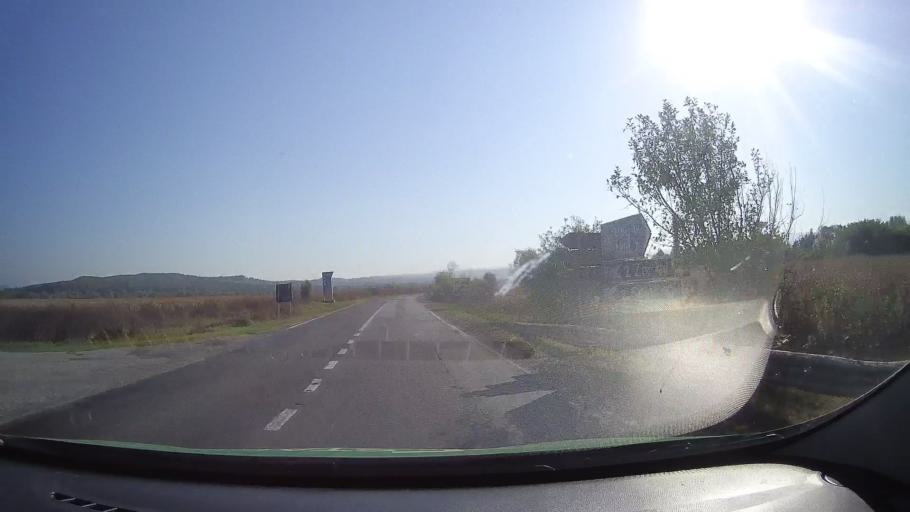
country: RO
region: Timis
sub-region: Comuna Margina
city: Margina
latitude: 45.8566
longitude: 22.2731
